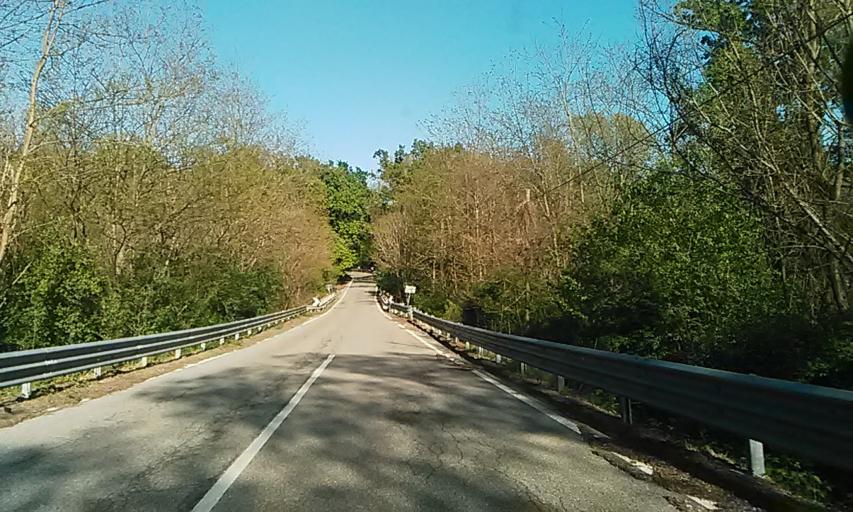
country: IT
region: Piedmont
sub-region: Provincia di Novara
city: Ghemme
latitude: 45.6135
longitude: 8.4433
